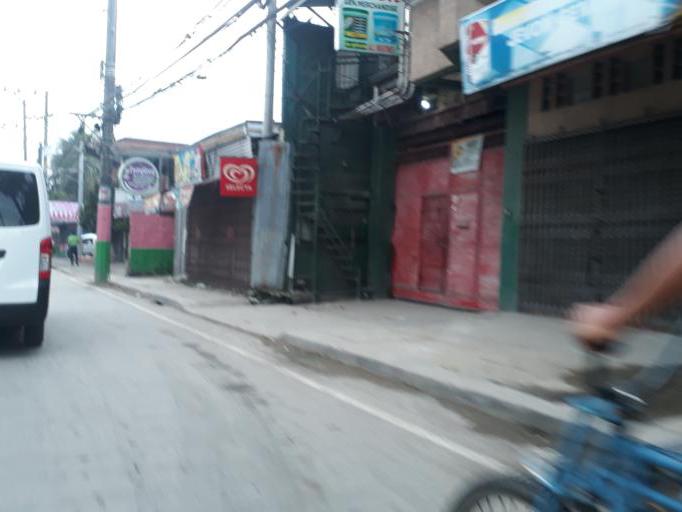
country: PH
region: Calabarzon
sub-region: Province of Rizal
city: Valenzuela
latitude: 14.6889
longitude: 120.9568
